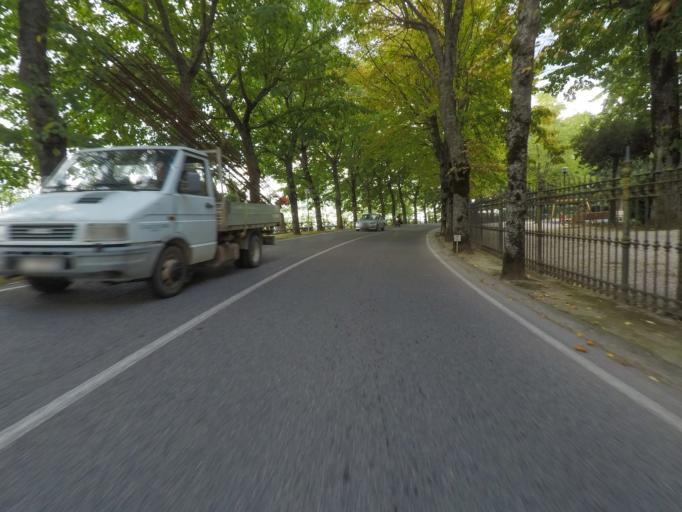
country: IT
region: Tuscany
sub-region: Provincia di Siena
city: Montepulciano
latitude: 43.0979
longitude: 11.7863
